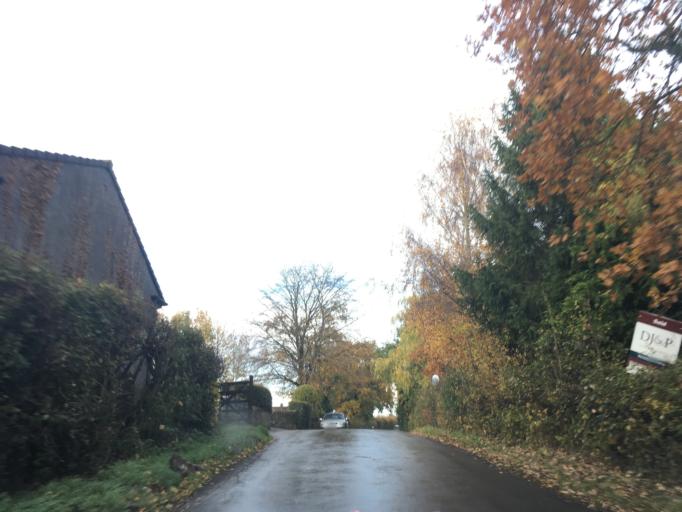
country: GB
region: England
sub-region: South Gloucestershire
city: Winterbourne
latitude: 51.5154
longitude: -2.4652
